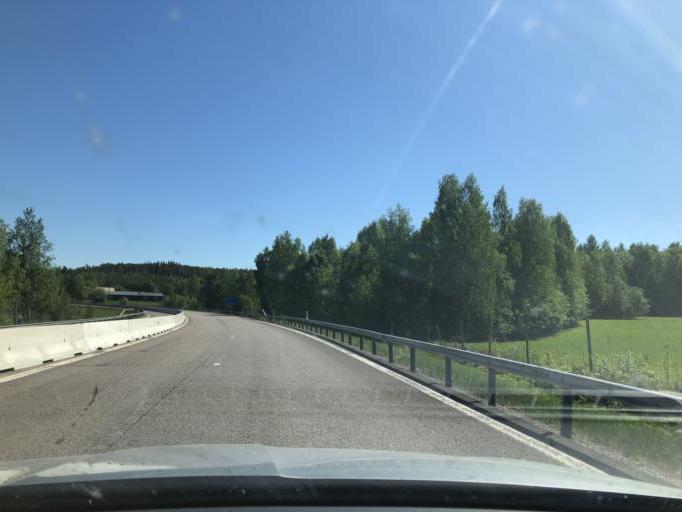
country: SE
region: Norrbotten
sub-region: Kalix Kommun
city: Rolfs
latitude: 65.8804
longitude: 22.9461
